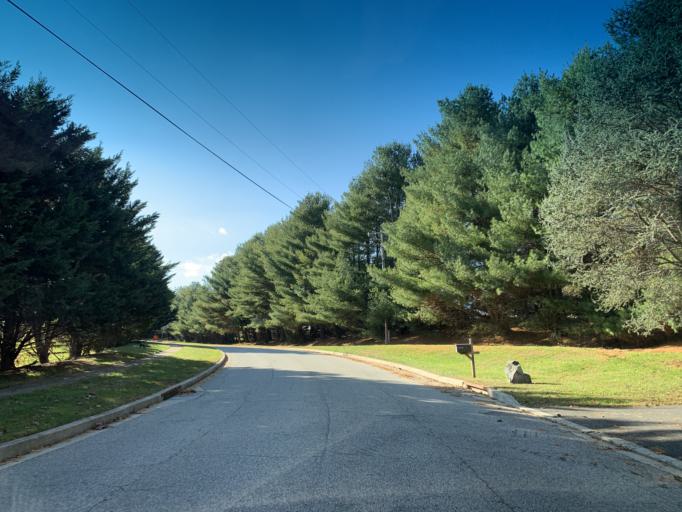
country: US
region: Maryland
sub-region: Harford County
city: Bel Air South
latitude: 39.5129
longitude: -76.3143
